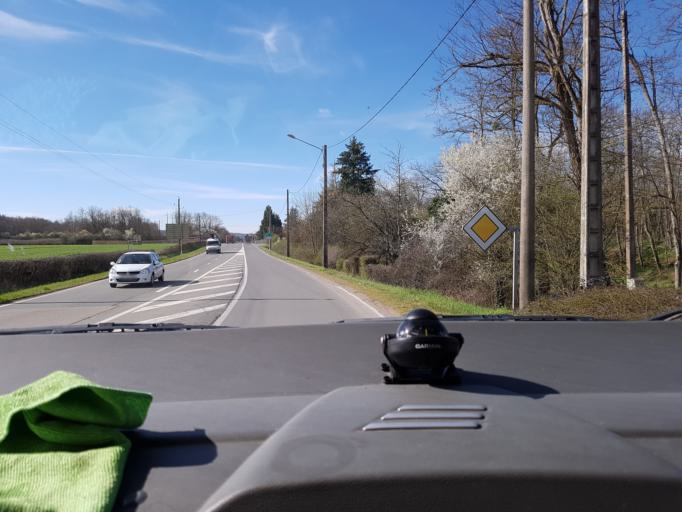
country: FR
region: Bourgogne
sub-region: Departement de Saone-et-Loire
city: Gueugnon
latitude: 46.5830
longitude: 4.0626
